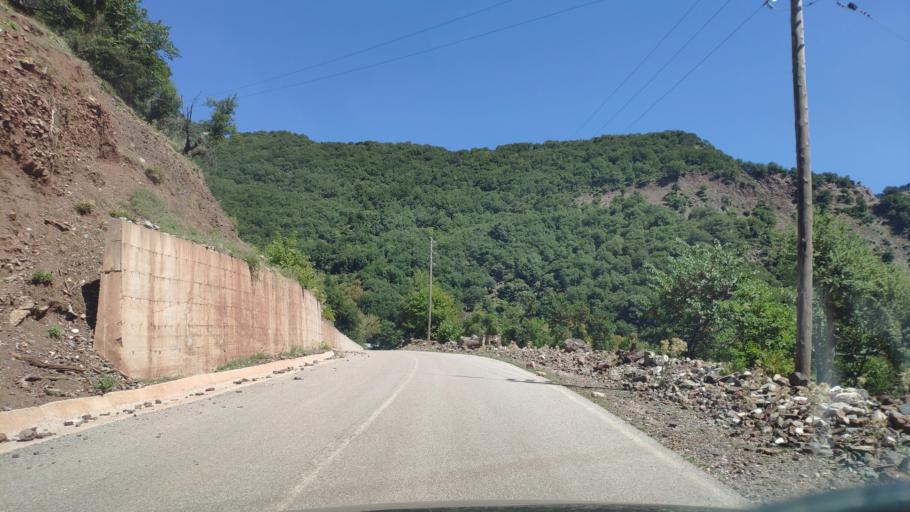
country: GR
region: Central Greece
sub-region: Nomos Evrytanias
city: Kerasochori
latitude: 39.0880
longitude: 21.5966
